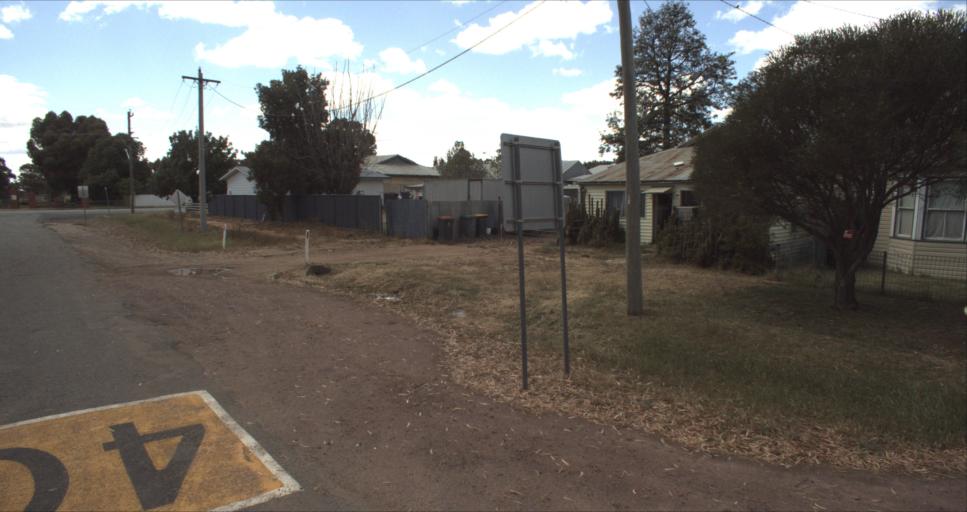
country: AU
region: New South Wales
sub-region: Murrumbidgee Shire
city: Darlington Point
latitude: -34.5183
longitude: 146.1819
